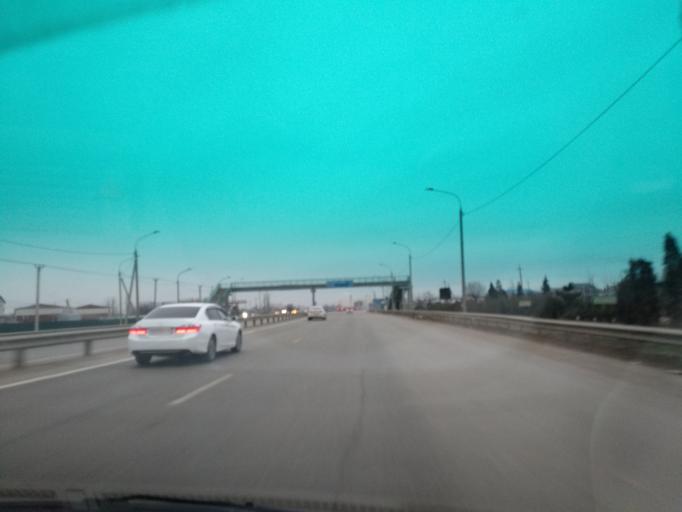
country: RU
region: Krasnodarskiy
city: Pashkovskiy
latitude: 45.0579
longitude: 39.1320
